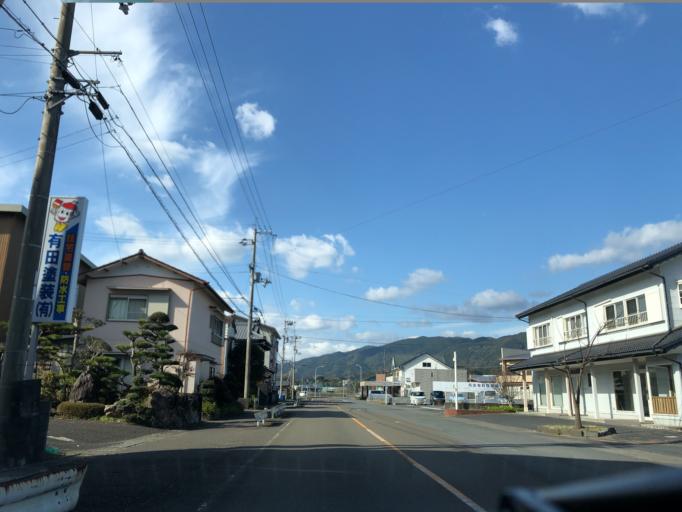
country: JP
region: Kochi
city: Sukumo
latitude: 32.9265
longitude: 132.7010
